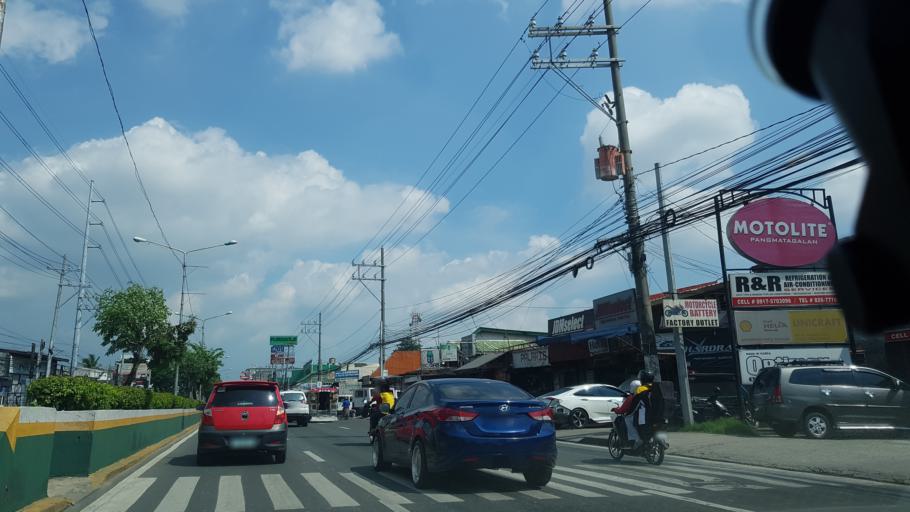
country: PH
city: Sambayanihan People's Village
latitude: 14.4675
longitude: 121.0142
